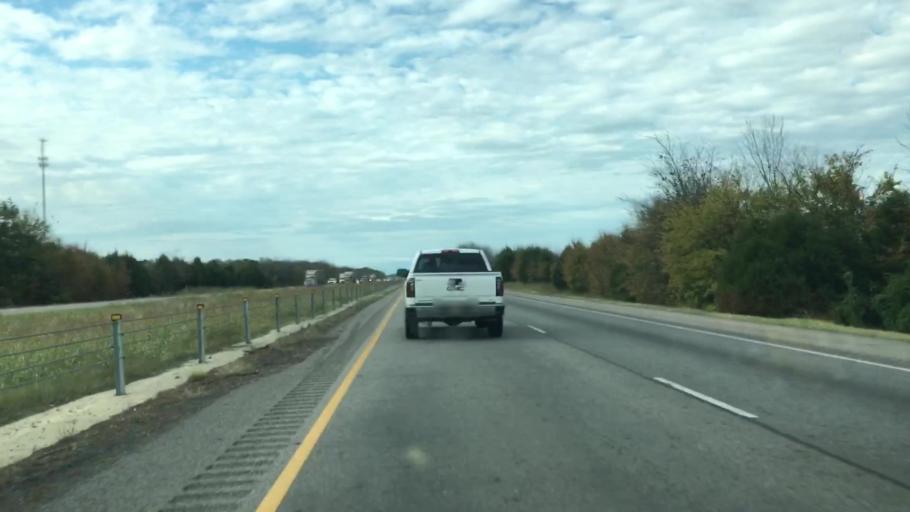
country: US
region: Arkansas
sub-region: Conway County
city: Morrilton
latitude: 35.2034
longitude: -92.8092
